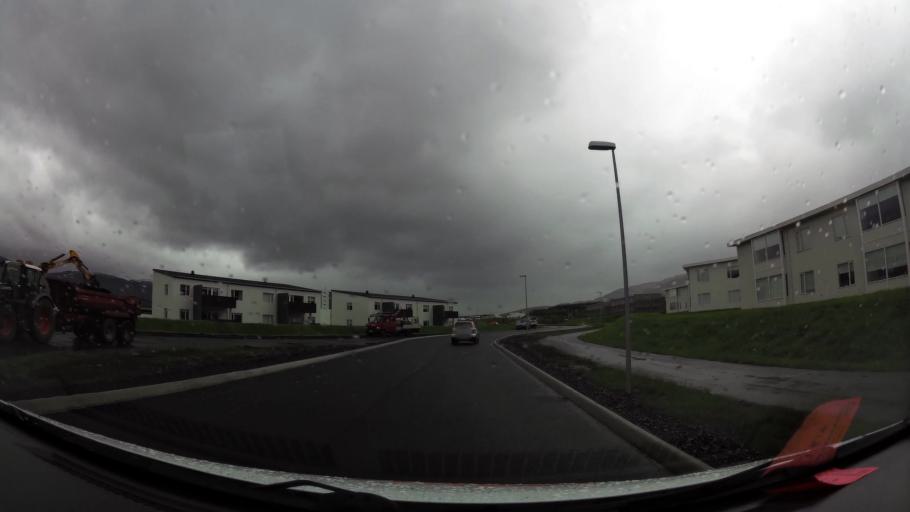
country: IS
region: Northeast
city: Akureyri
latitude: 65.6682
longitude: -18.1080
